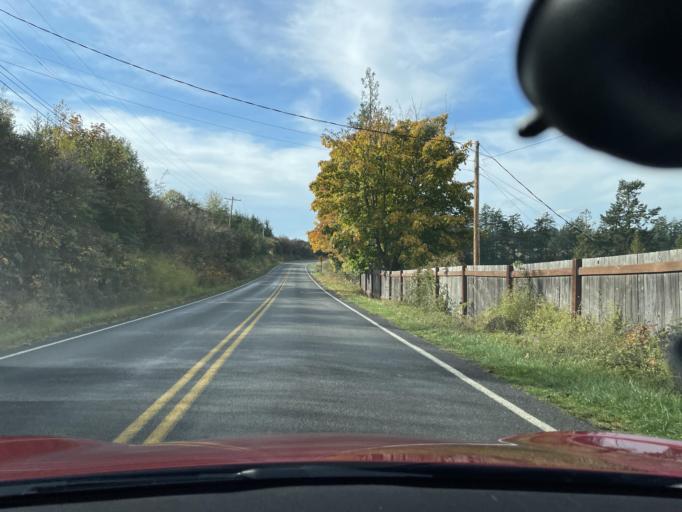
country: US
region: Washington
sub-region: San Juan County
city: Friday Harbor
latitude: 48.5257
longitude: -122.9966
